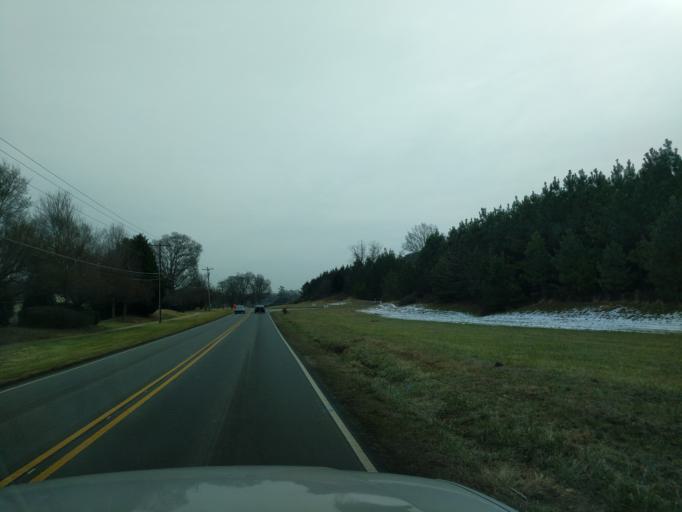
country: US
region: North Carolina
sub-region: Mecklenburg County
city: Charlotte
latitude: 35.3053
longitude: -80.8655
